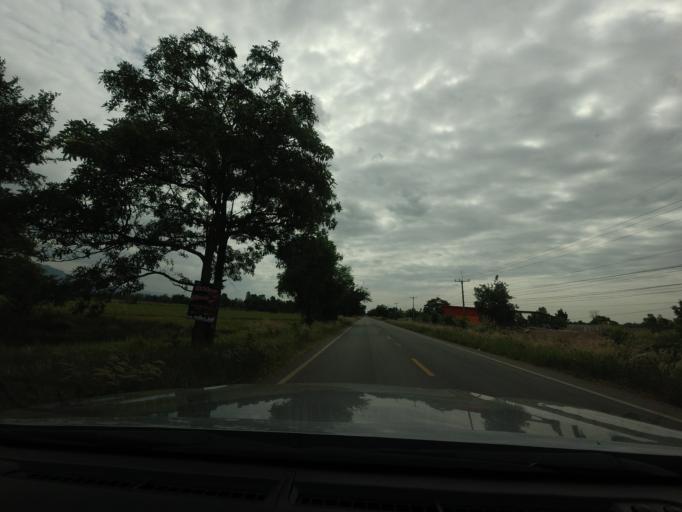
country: TH
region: Phitsanulok
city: Noen Maprang
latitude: 16.6666
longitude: 100.6148
